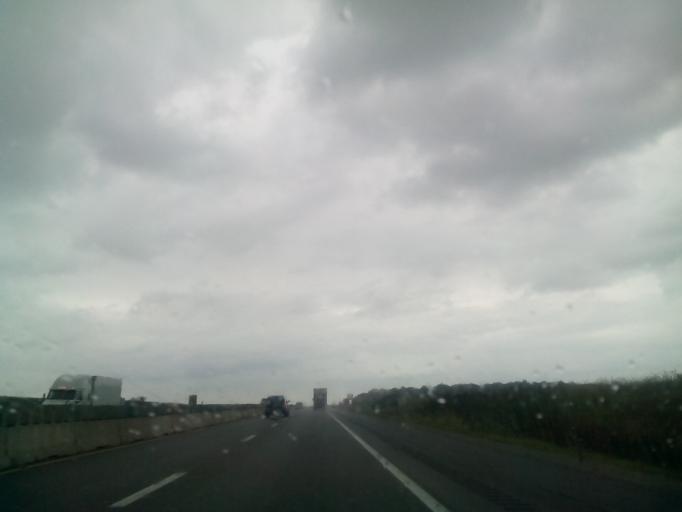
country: US
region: Ohio
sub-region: Huron County
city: Bellevue
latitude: 41.3529
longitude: -82.8700
